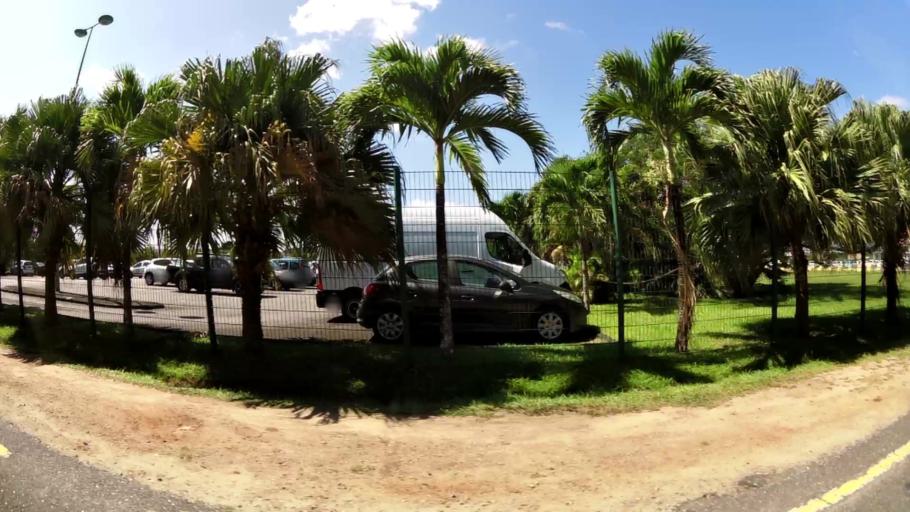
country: GF
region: Guyane
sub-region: Guyane
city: Matoury
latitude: 4.8249
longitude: -52.3646
